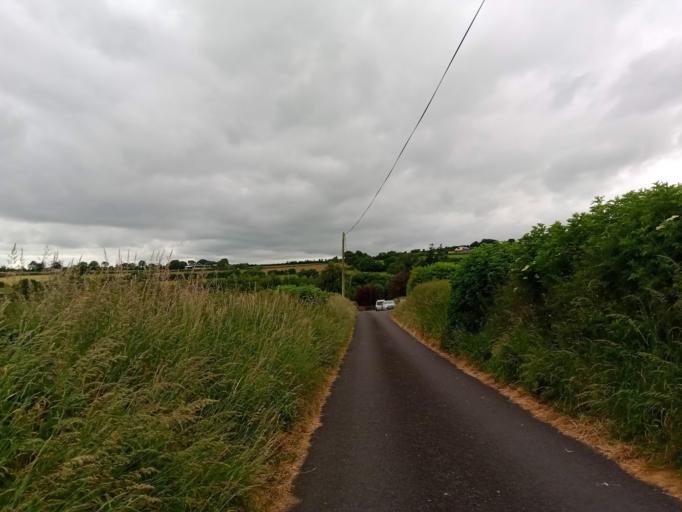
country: IE
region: Leinster
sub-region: Laois
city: Rathdowney
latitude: 52.7689
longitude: -7.4698
